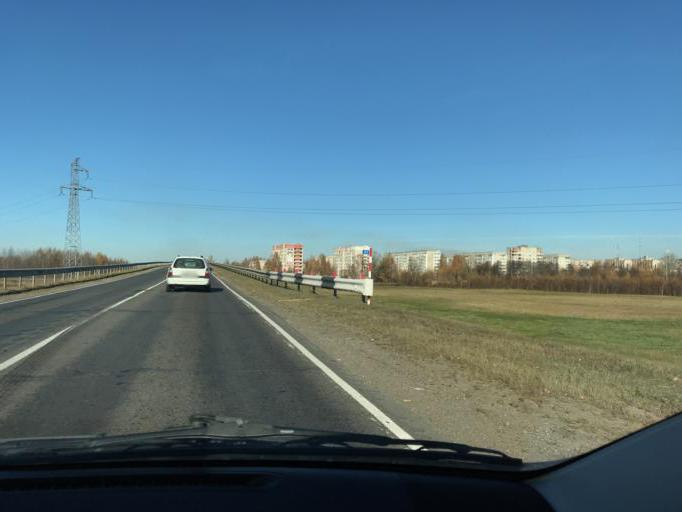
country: BY
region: Vitebsk
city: Polatsk
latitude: 55.4613
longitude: 28.7610
